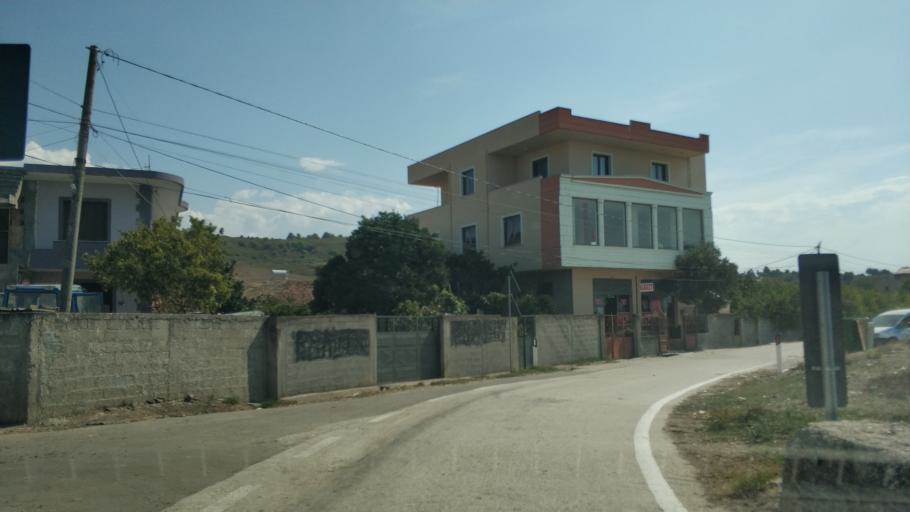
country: AL
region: Fier
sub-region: Rrethi i Fierit
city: Dermenas
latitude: 40.7285
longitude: 19.4689
